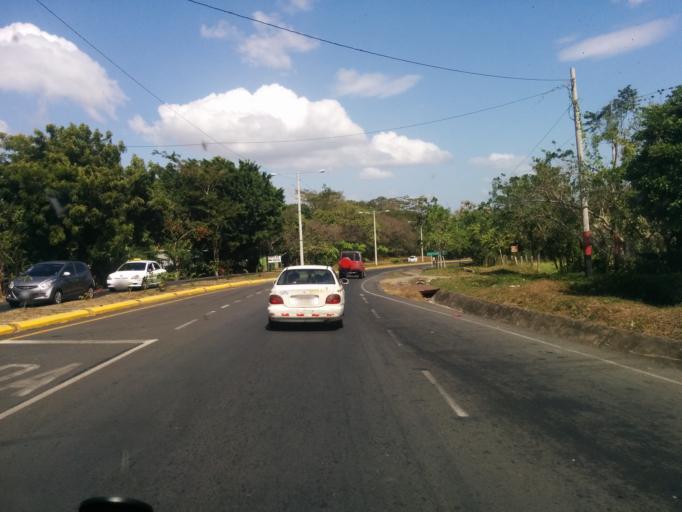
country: NI
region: Masaya
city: Masaya
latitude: 11.9567
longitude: -86.0915
